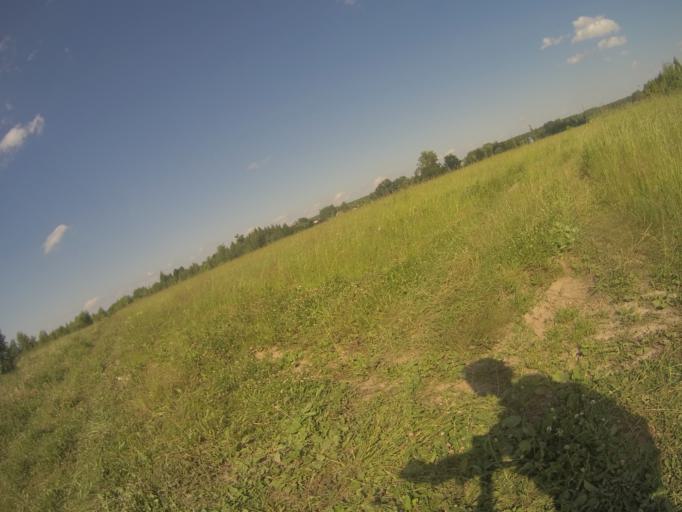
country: RU
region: Vladimir
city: Stavrovo
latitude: 56.2098
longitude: 40.1107
